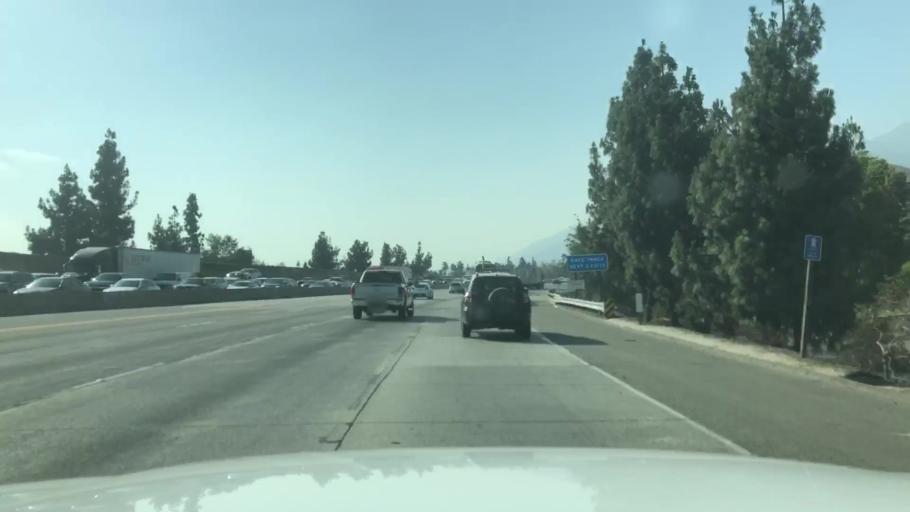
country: US
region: California
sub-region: Los Angeles County
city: Monrovia
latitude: 34.1379
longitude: -118.0137
